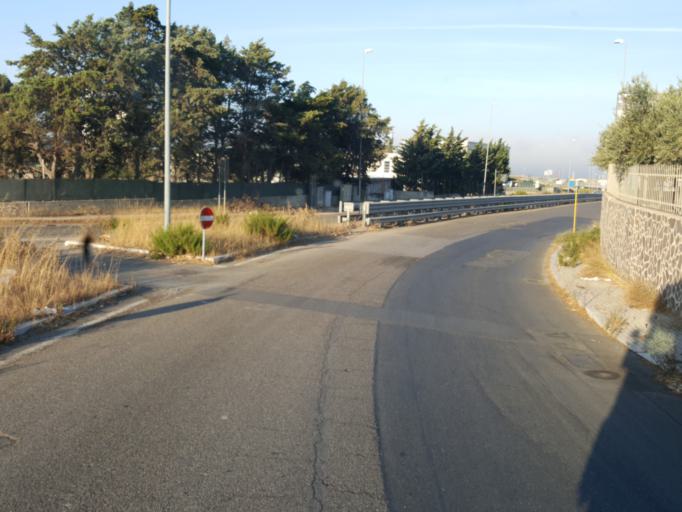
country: IT
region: Latium
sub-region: Citta metropolitana di Roma Capitale
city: Aurelia
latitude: 42.1203
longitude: 11.7780
